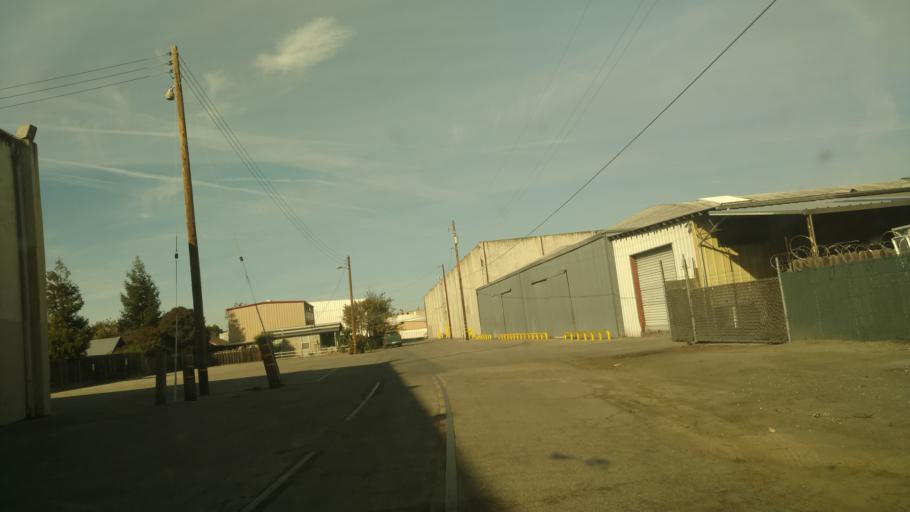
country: US
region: California
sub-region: San Benito County
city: Hollister
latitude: 36.8470
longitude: -121.3970
